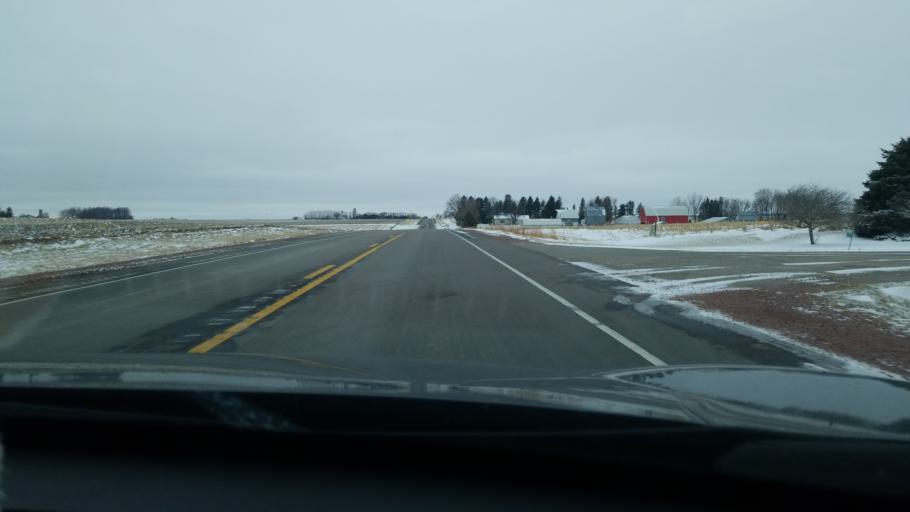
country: US
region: Iowa
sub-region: Lyon County
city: Rock Rapids
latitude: 43.4330
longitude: -96.3737
